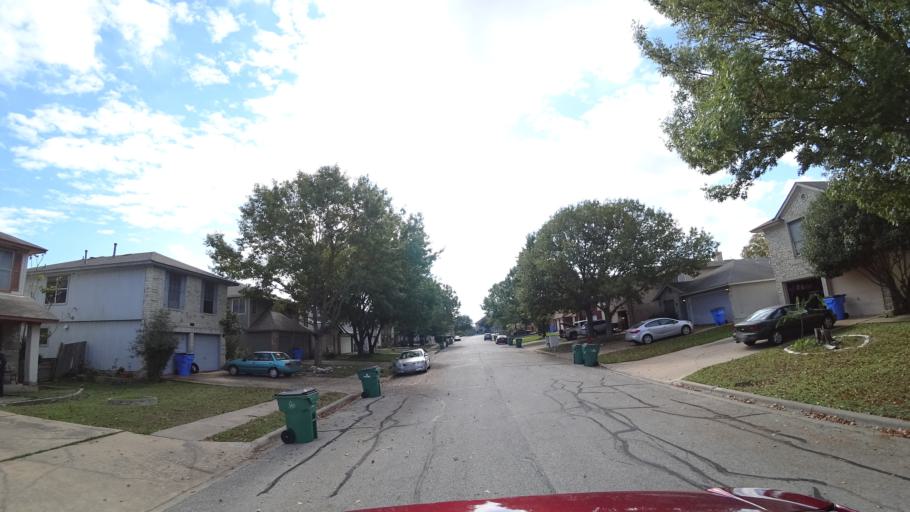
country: US
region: Texas
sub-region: Travis County
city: Pflugerville
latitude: 30.4373
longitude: -97.6368
